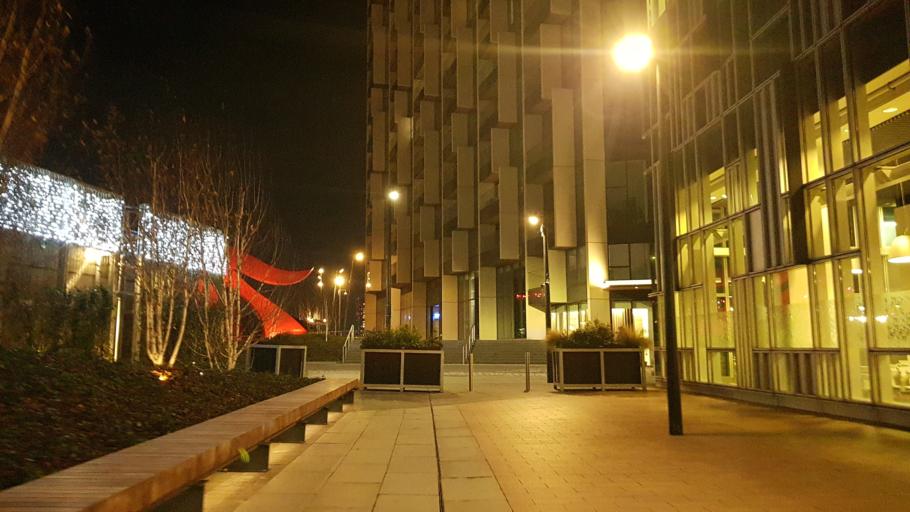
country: GB
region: England
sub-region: Greater London
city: Poplar
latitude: 51.5013
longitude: 0.0064
